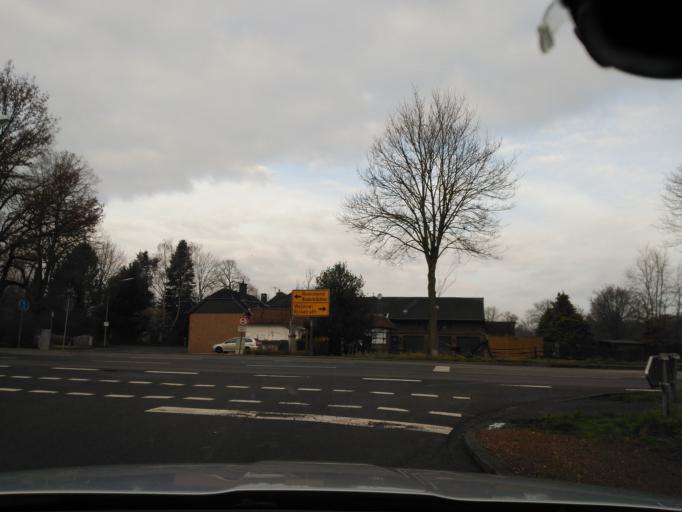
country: DE
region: North Rhine-Westphalia
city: Wegberg
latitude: 51.1504
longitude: 6.2735
